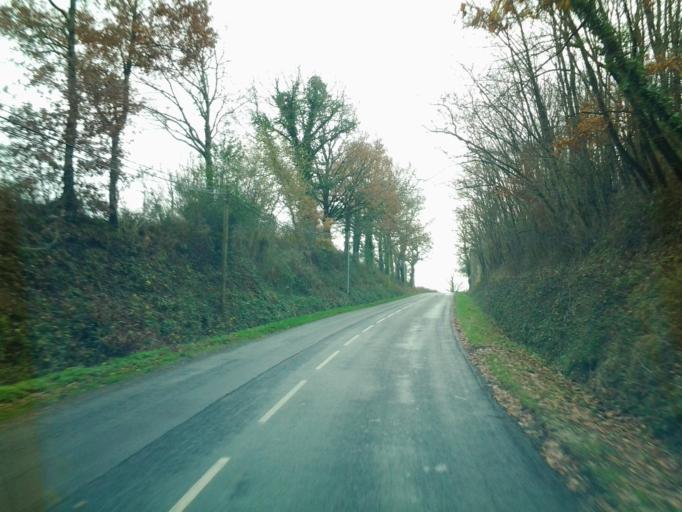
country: FR
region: Pays de la Loire
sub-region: Departement de la Vendee
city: La Roche-sur-Yon
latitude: 46.6582
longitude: -1.3960
